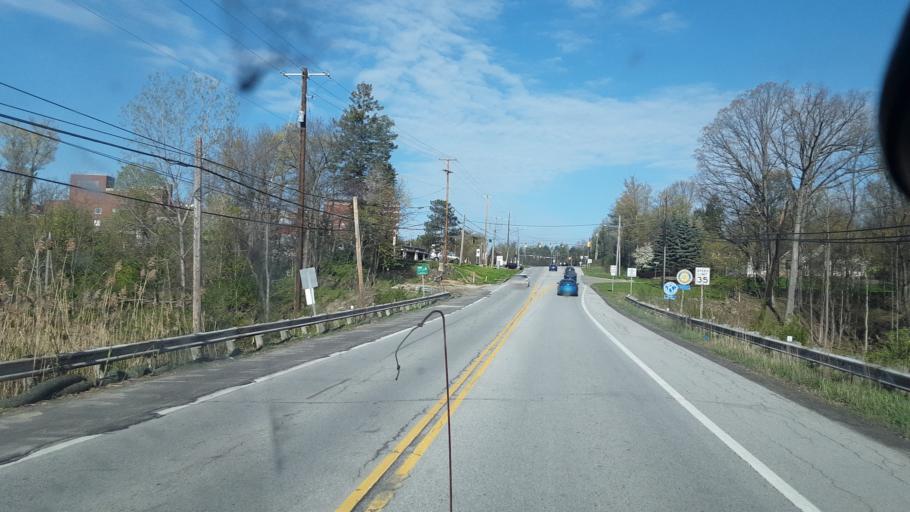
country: US
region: Ohio
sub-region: Medina County
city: Medina
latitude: 41.1387
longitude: -81.8353
